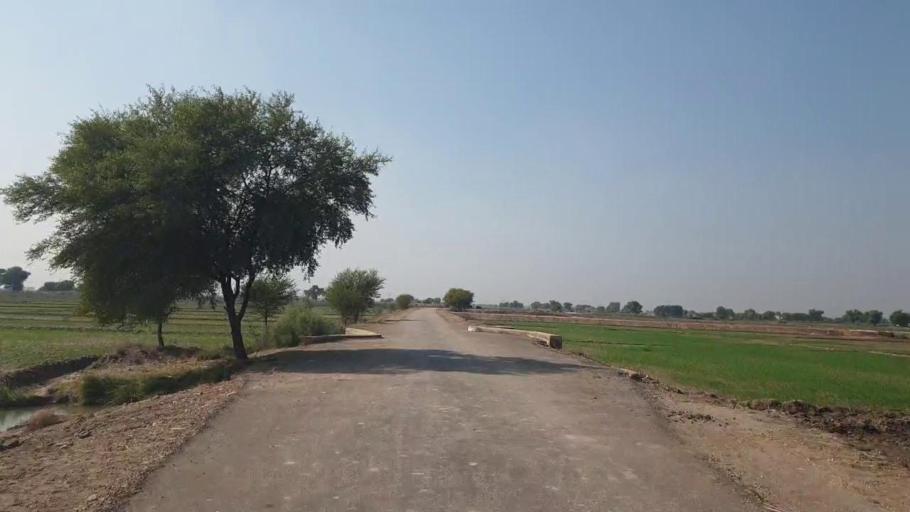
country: PK
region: Sindh
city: Sehwan
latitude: 26.4274
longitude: 67.8257
